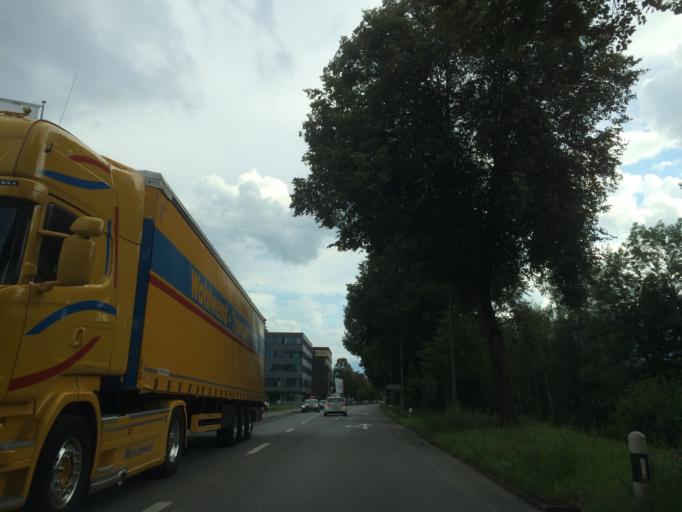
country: CH
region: Saint Gallen
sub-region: Wahlkreis Werdenberg
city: Haag (Rheintal)
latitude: 47.2075
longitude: 9.5021
